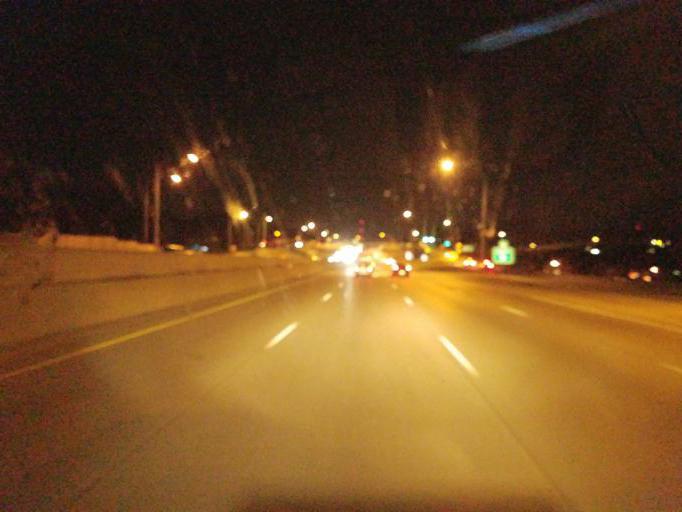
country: US
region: Iowa
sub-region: Polk County
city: Windsor Heights
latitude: 41.5931
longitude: -93.6635
